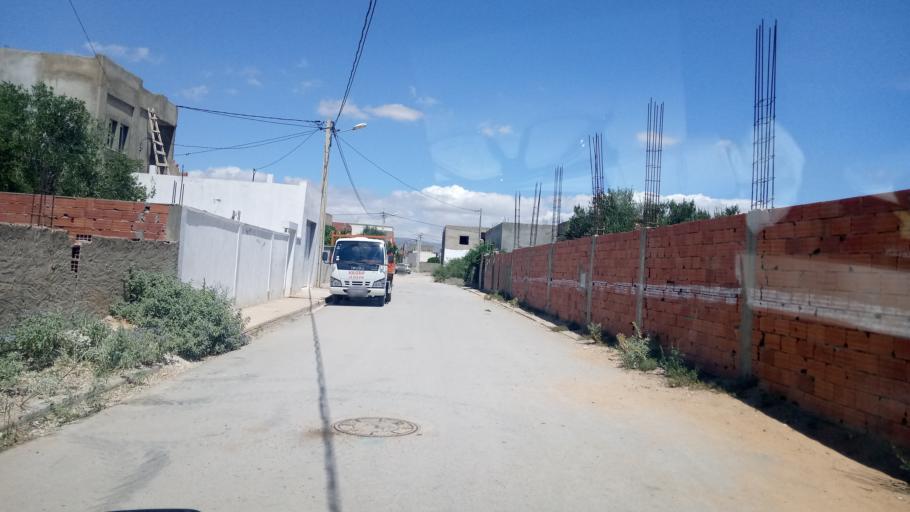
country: TN
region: Al Qayrawan
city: Sbikha
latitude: 36.1262
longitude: 10.0902
